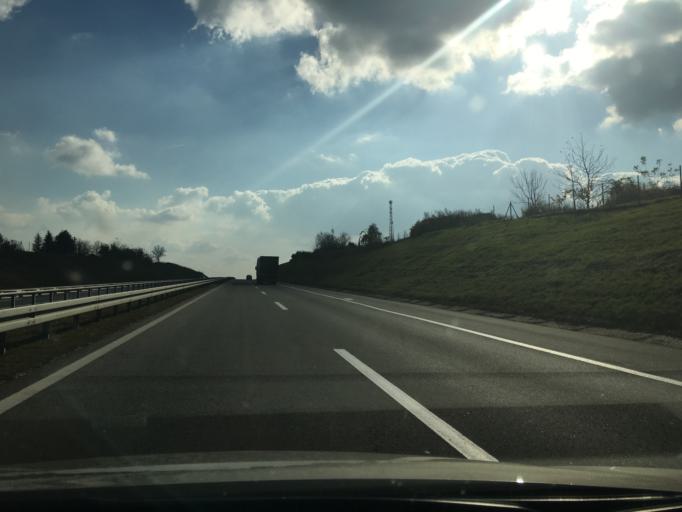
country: RS
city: Beska
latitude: 45.1619
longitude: 20.0808
